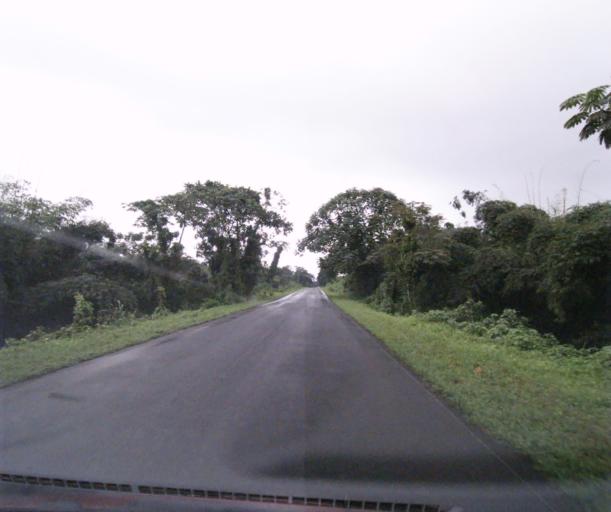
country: CM
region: South-West Province
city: Idenao
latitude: 4.1279
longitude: 8.9886
